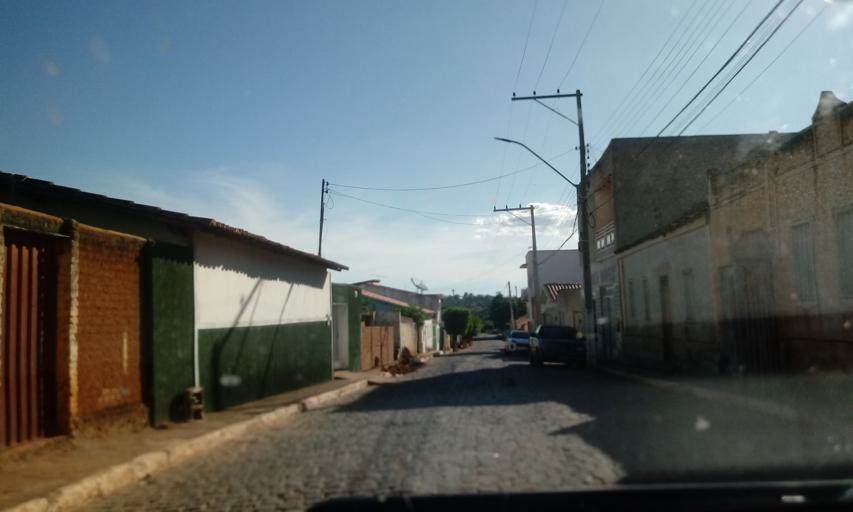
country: BR
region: Bahia
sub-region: Riacho De Santana
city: Riacho de Santana
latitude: -13.7721
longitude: -42.7142
